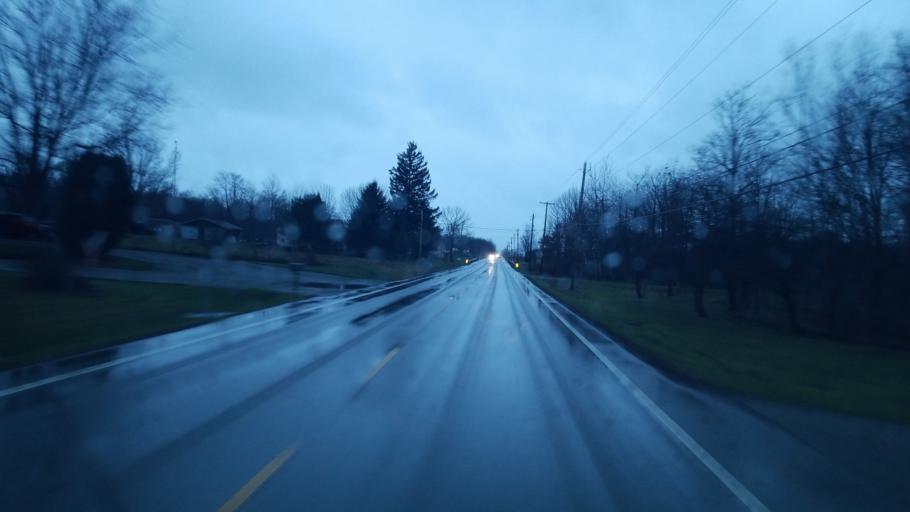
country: US
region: Ohio
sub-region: Ashtabula County
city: Andover
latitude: 41.6070
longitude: -80.6690
